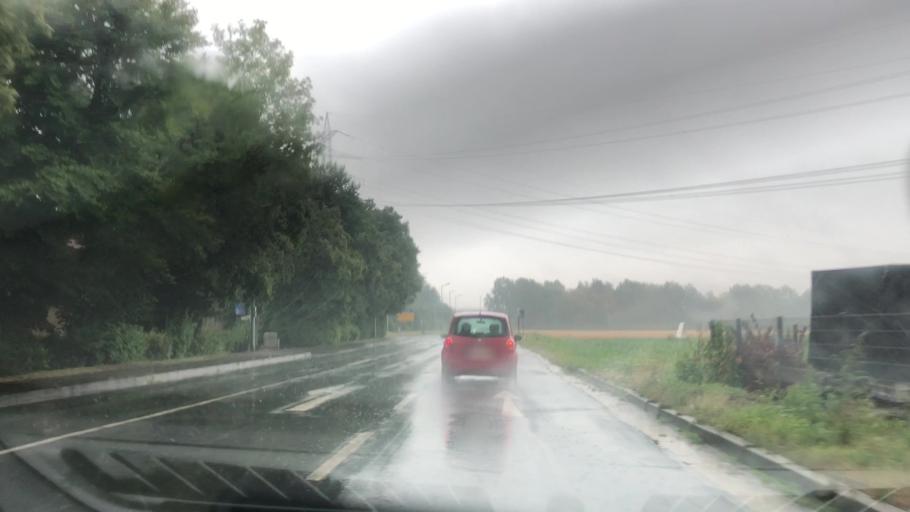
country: DE
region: North Rhine-Westphalia
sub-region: Regierungsbezirk Detmold
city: Minden
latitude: 52.2774
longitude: 8.9627
